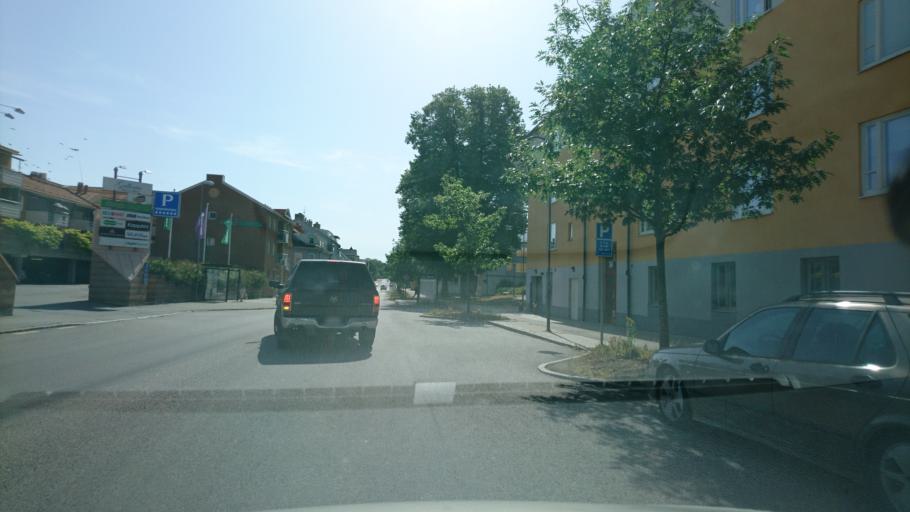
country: SE
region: Soedermanland
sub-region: Strangnas Kommun
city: Strangnas
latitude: 59.3757
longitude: 17.0256
